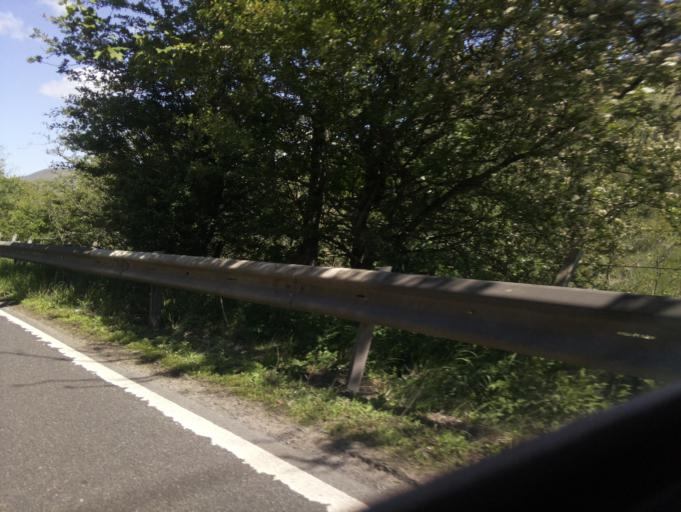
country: GB
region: Scotland
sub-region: Dumfries and Galloway
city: Langholm
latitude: 55.2353
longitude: -2.9753
